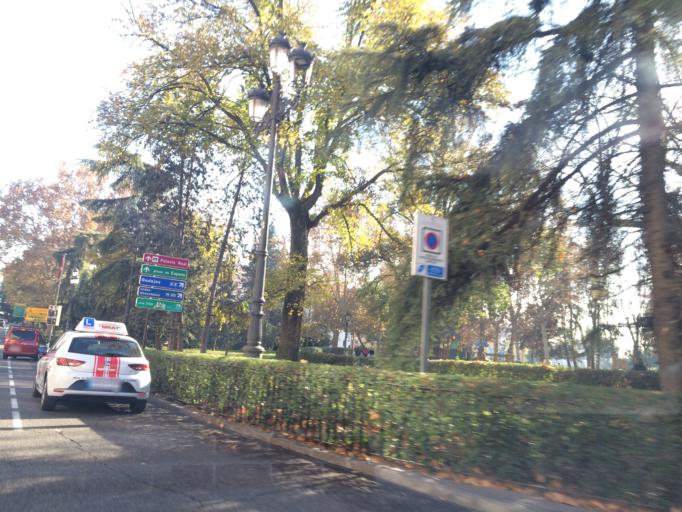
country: ES
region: Madrid
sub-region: Provincia de Madrid
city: City Center
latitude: 40.4243
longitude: -3.7157
